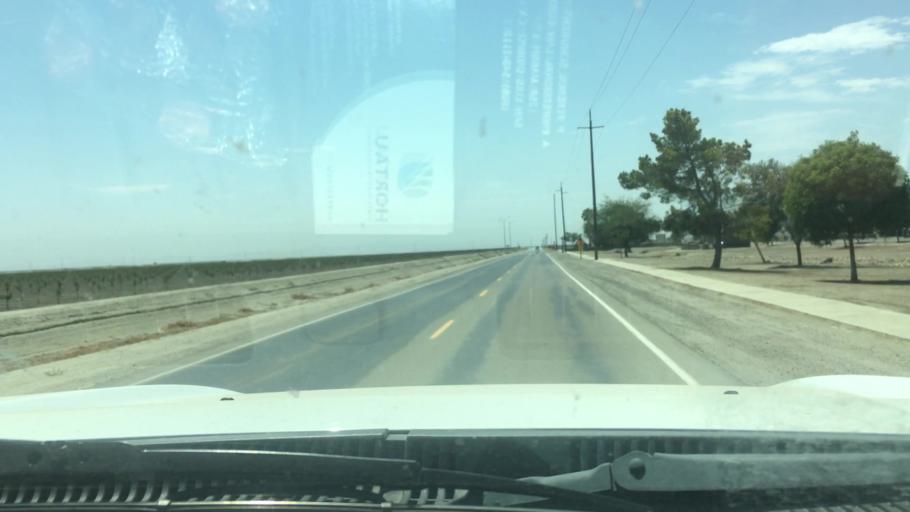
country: US
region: California
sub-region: Kings County
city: Corcoran
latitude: 36.0508
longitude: -119.5548
